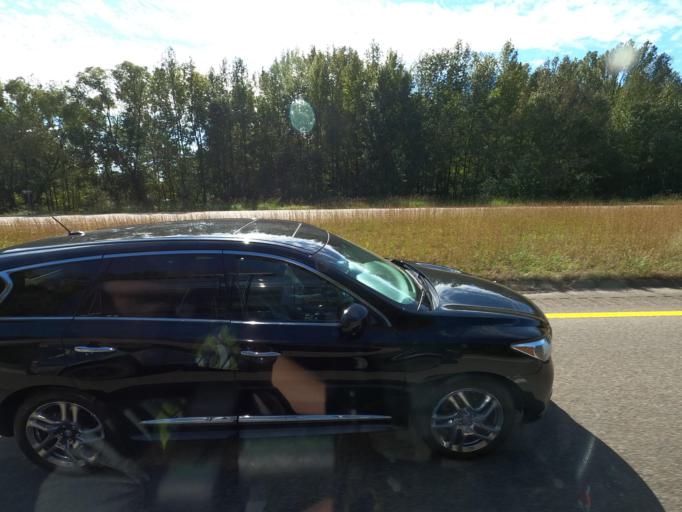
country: US
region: Tennessee
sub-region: Madison County
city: Jackson
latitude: 35.6682
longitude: -88.9097
